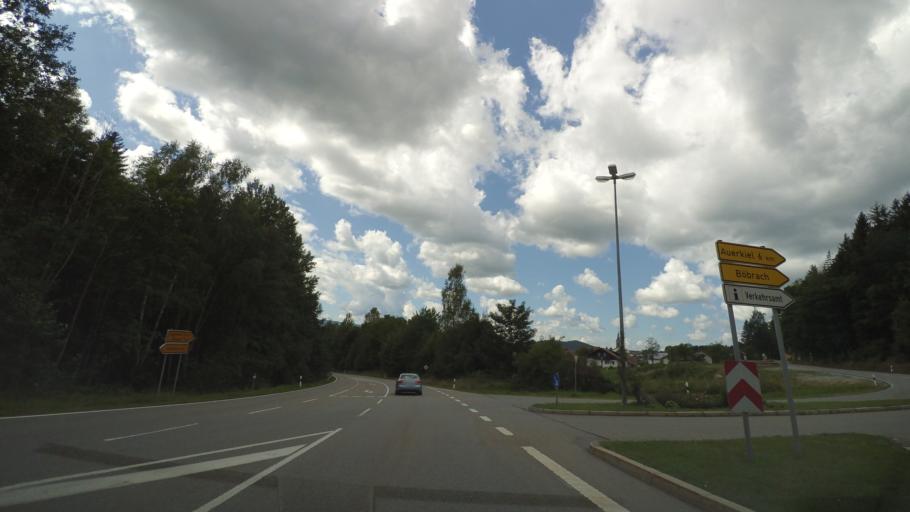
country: DE
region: Bavaria
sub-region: Lower Bavaria
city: Bobrach
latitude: 49.0552
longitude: 13.0422
